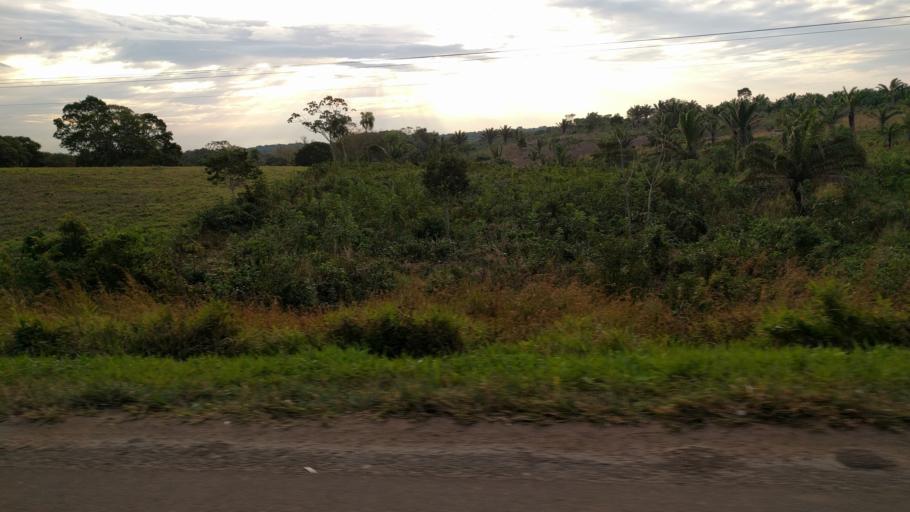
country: BO
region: Santa Cruz
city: Buena Vista
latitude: -17.4409
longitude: -63.6447
